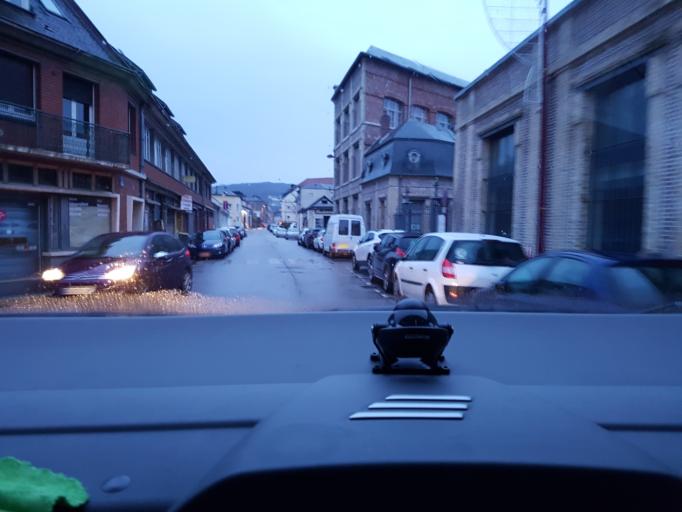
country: FR
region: Haute-Normandie
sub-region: Departement de la Seine-Maritime
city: Elbeuf
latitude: 49.2877
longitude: 1.0065
